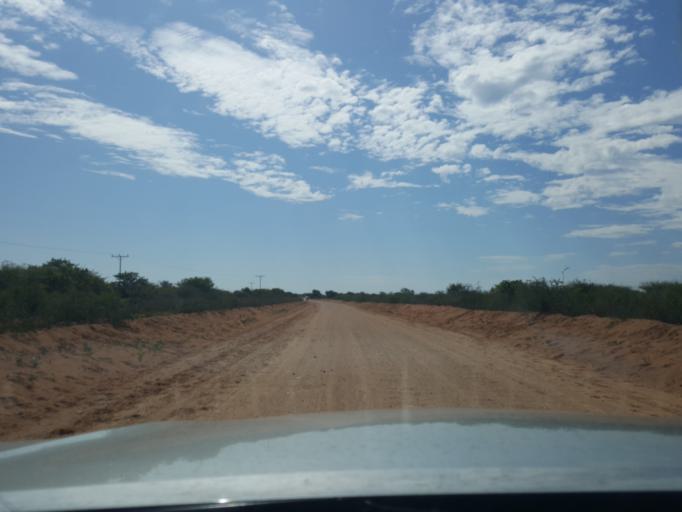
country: BW
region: Kweneng
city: Khudumelapye
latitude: -23.8515
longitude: 24.8728
